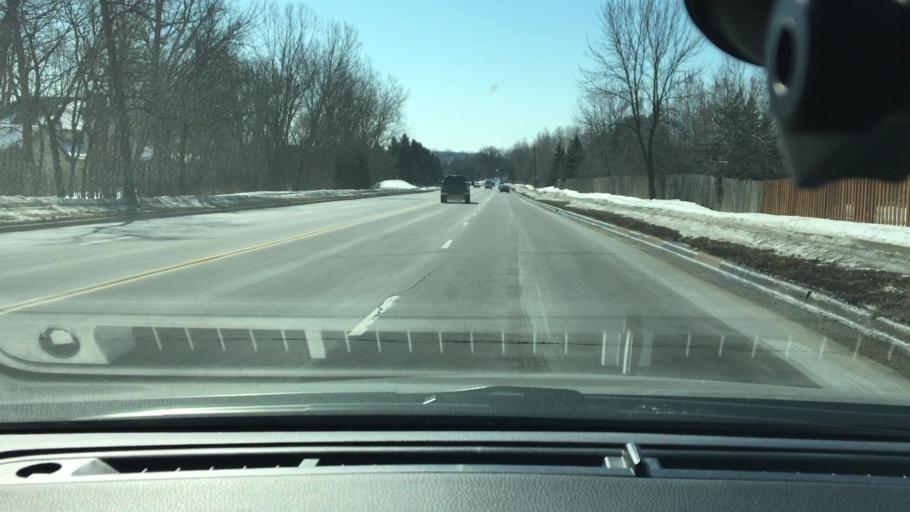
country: US
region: Minnesota
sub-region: Hennepin County
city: Maple Grove
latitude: 45.0549
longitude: -93.4463
